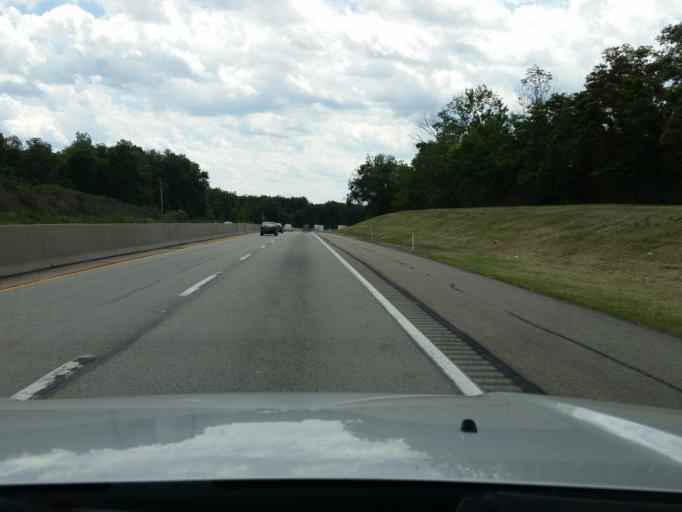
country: US
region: Pennsylvania
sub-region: Franklin County
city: Doylestown
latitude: 40.1310
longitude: -77.7420
